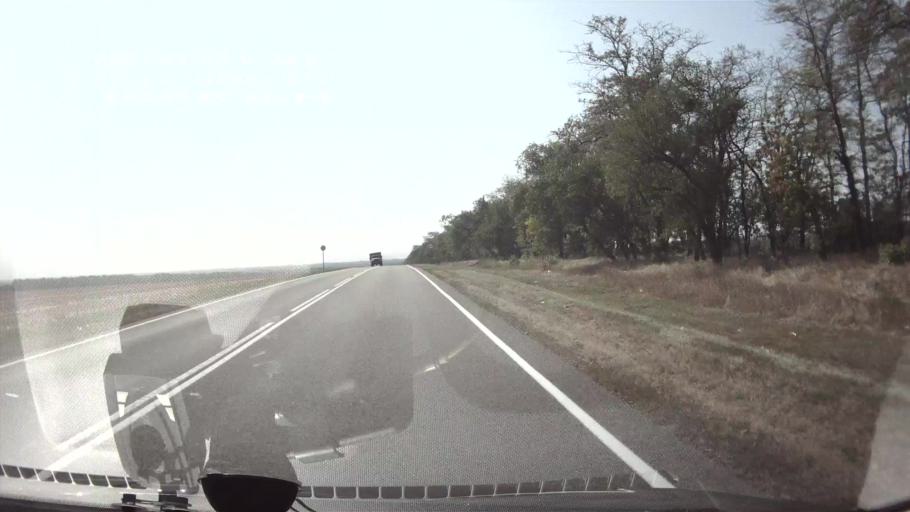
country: RU
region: Krasnodarskiy
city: Dmitriyevskaya
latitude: 45.7746
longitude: 40.7195
